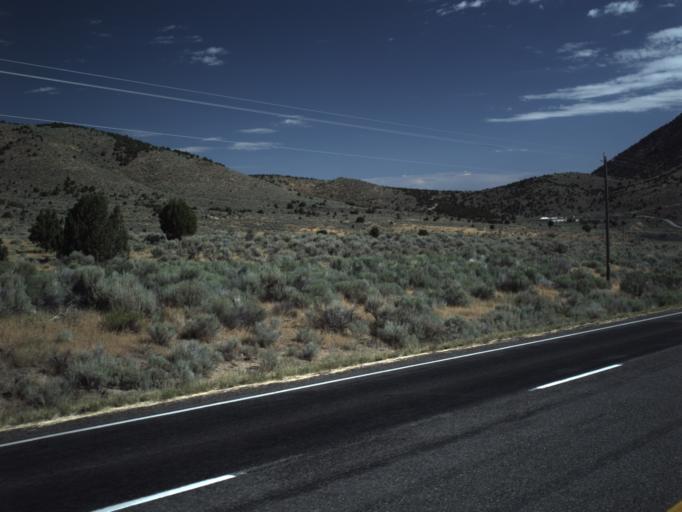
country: US
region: Utah
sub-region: Utah County
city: Genola
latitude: 39.9677
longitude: -112.0904
